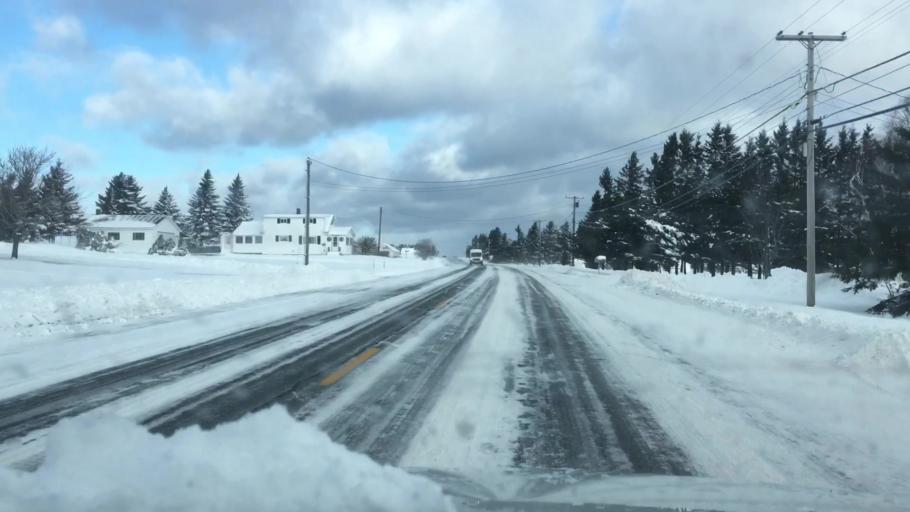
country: US
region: Maine
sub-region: Aroostook County
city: Caribou
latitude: 46.9055
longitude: -68.0158
